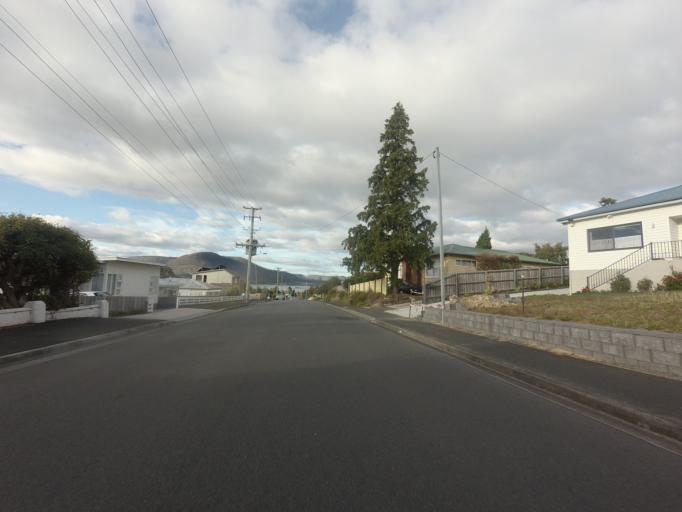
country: AU
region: Tasmania
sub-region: Glenorchy
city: Glenorchy
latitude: -42.8272
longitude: 147.2627
